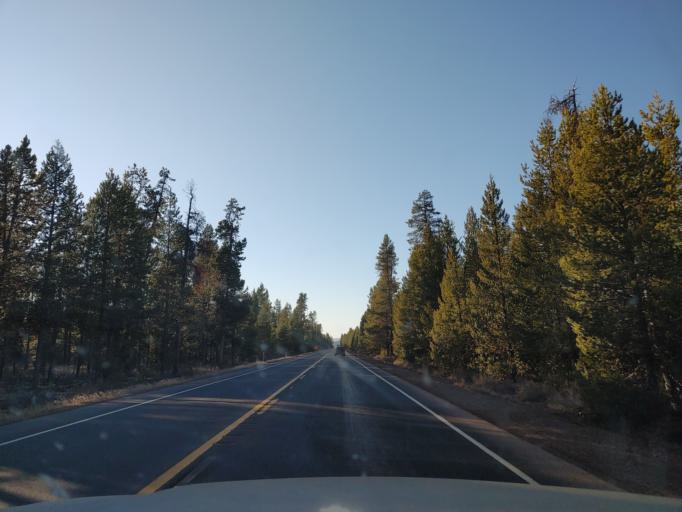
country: US
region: Oregon
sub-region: Deschutes County
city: La Pine
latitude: 43.3843
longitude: -121.8050
